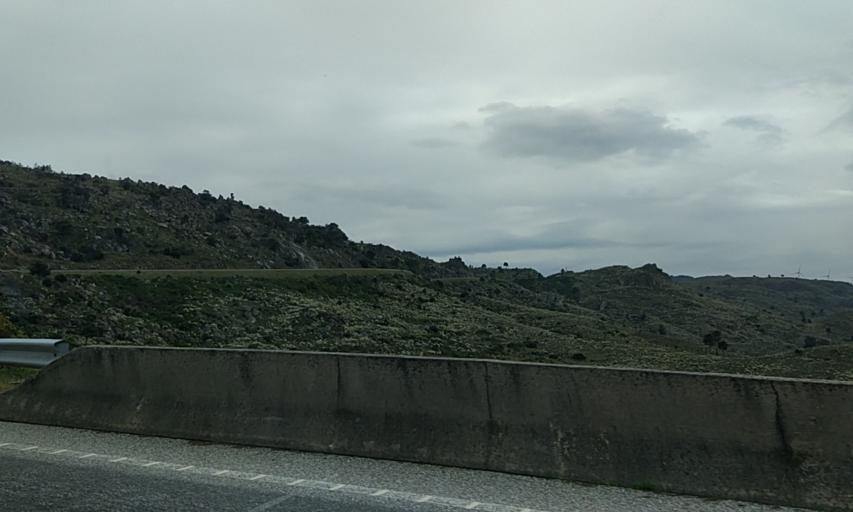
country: PT
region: Guarda
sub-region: Guarda
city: Guarda
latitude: 40.6015
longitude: -7.2790
